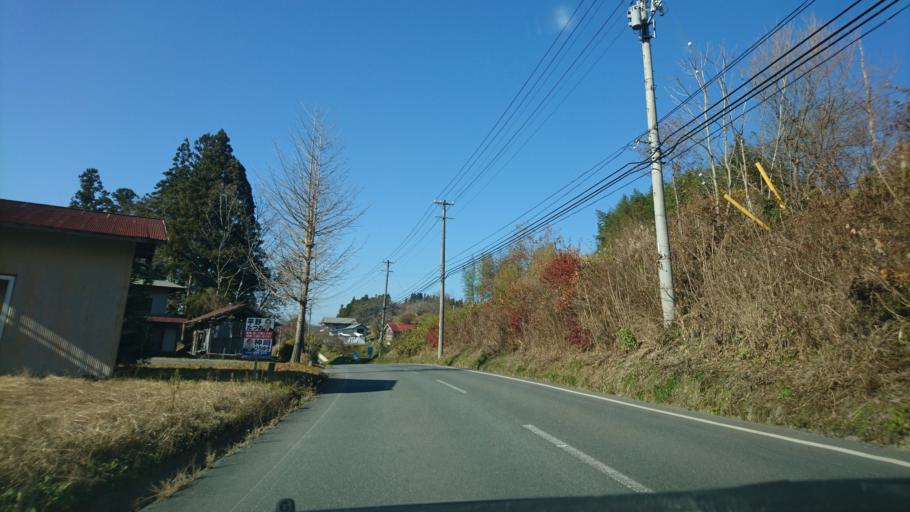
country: JP
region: Iwate
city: Ichinoseki
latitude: 38.9058
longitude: 141.3614
